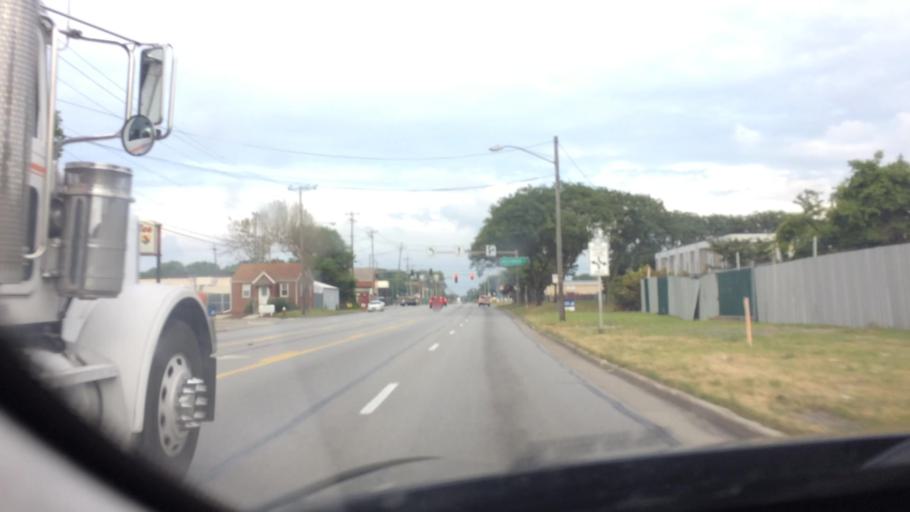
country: US
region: Ohio
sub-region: Lucas County
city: Ottawa Hills
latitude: 41.6380
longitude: -83.6088
